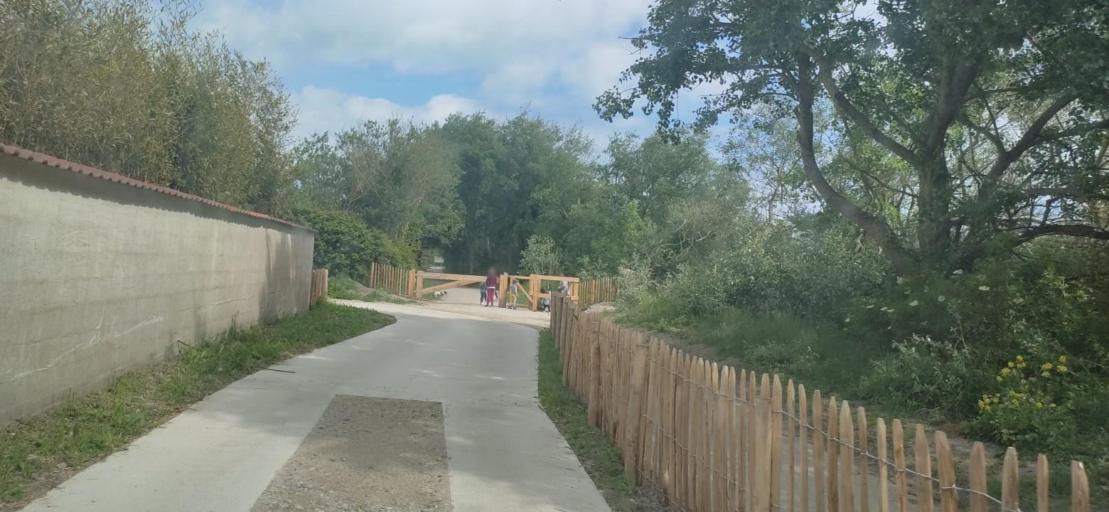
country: FR
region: Nord-Pas-de-Calais
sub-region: Departement du Pas-de-Calais
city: Oye-Plage
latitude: 51.0035
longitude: 2.0674
